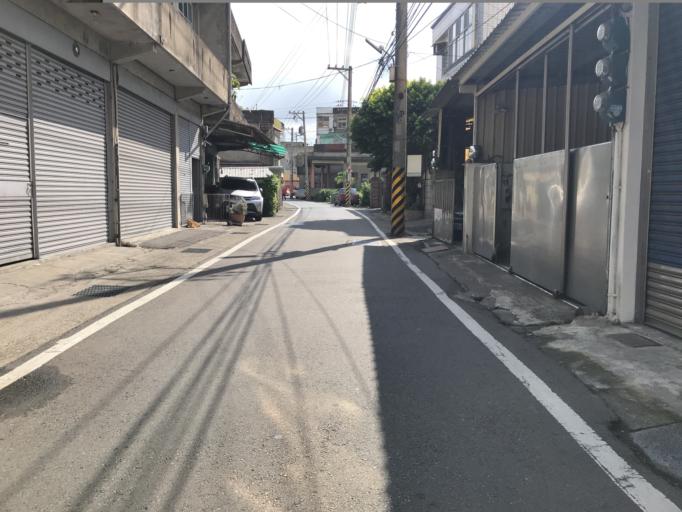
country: TW
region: Taiwan
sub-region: Hsinchu
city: Zhubei
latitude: 24.8118
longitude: 121.0009
